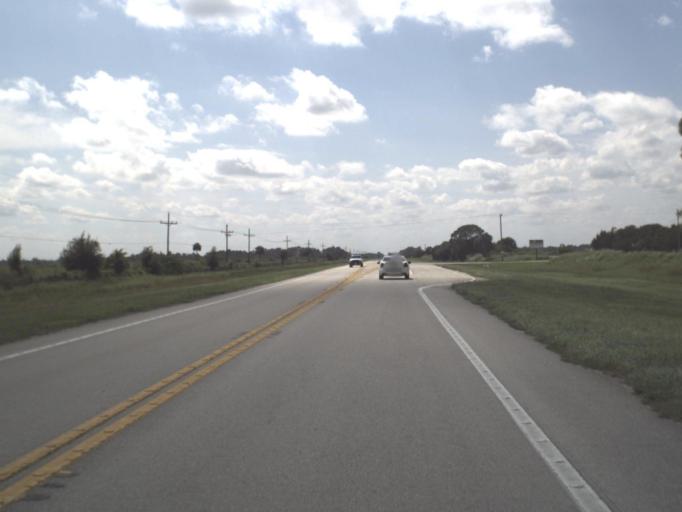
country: US
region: Florida
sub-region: Hendry County
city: Port LaBelle
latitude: 26.6387
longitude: -81.4363
